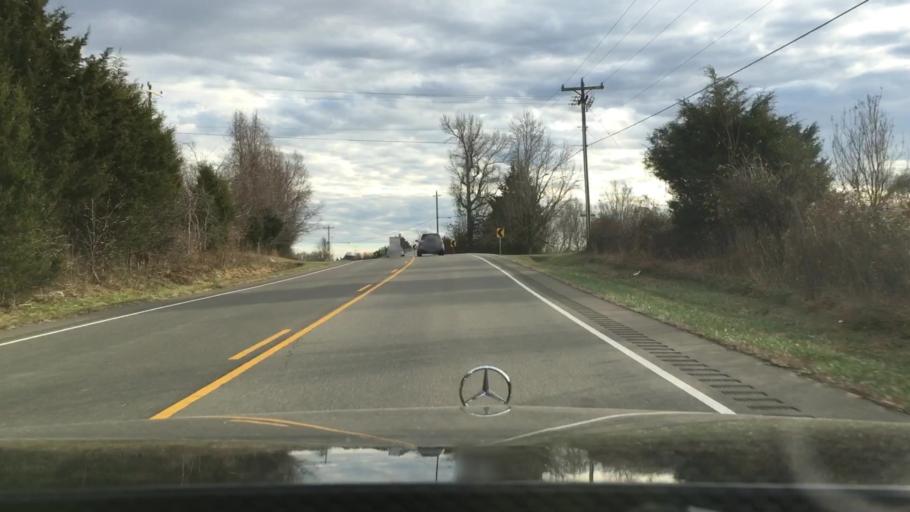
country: US
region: North Carolina
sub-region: Orange County
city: Hillsborough
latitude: 36.1599
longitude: -79.1297
